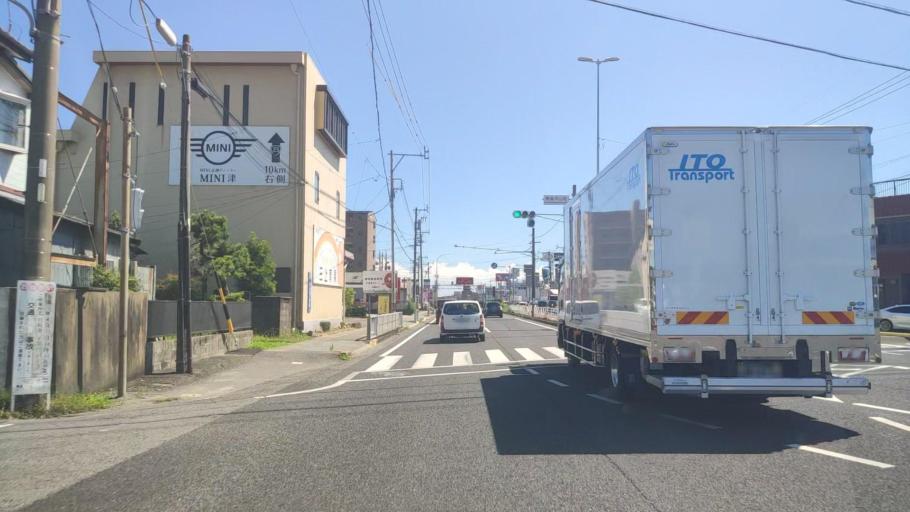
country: JP
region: Mie
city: Tsu-shi
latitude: 34.7560
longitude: 136.5231
